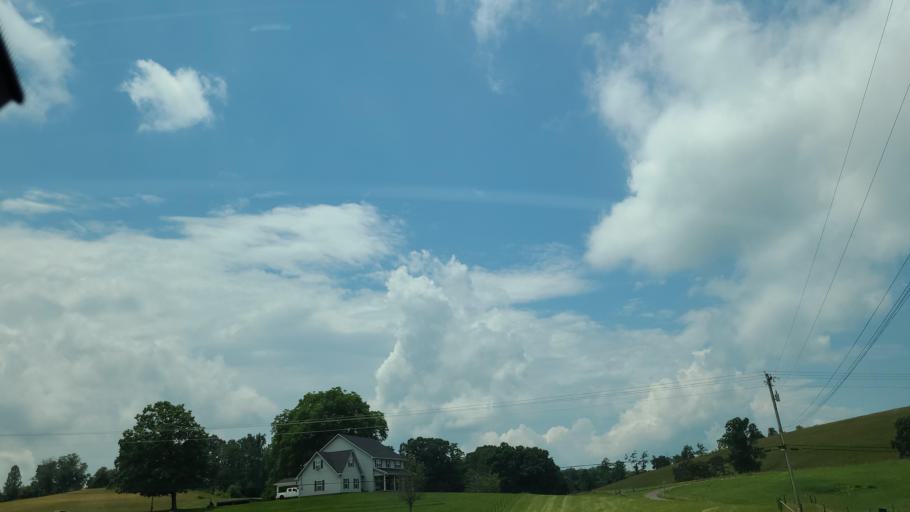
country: US
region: Tennessee
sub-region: Hamblen County
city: Morristown
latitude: 36.1584
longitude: -83.3523
